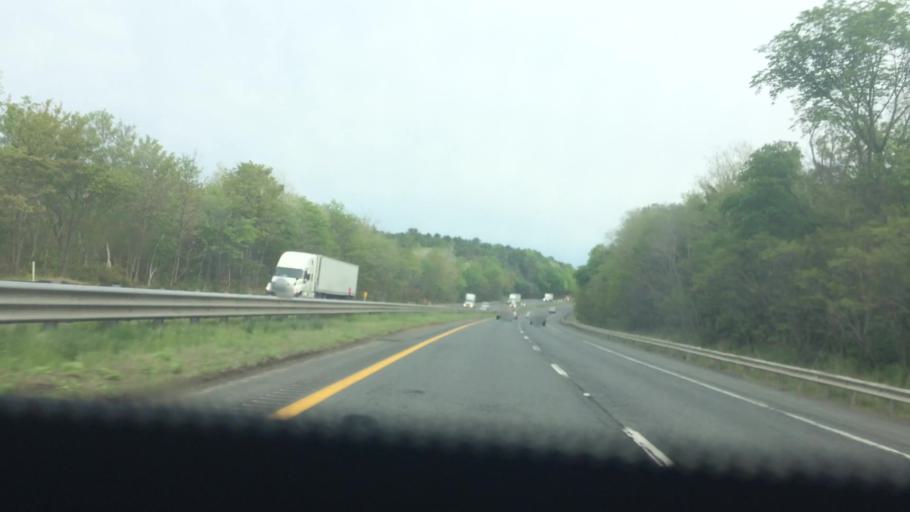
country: US
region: Massachusetts
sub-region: Worcester County
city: Fiskdale
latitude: 42.1365
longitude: -72.1286
